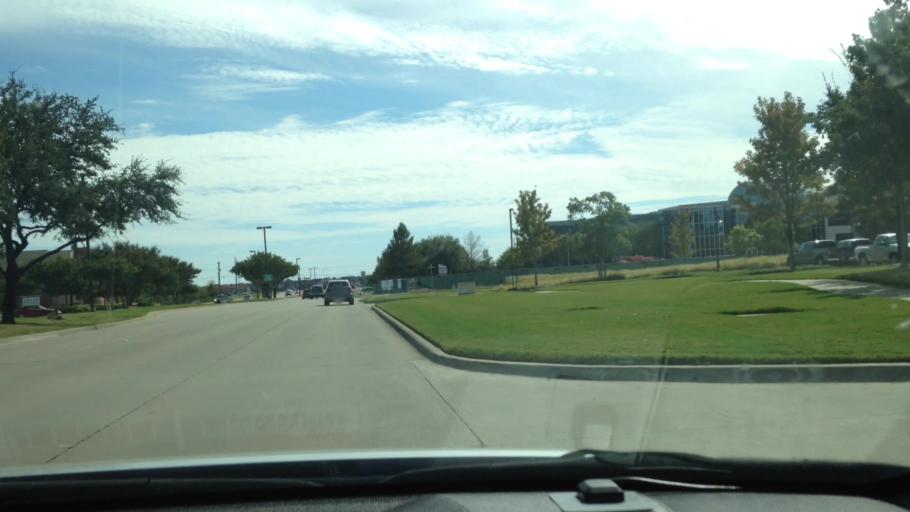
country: US
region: Texas
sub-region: Denton County
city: The Colony
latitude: 33.0696
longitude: -96.8188
